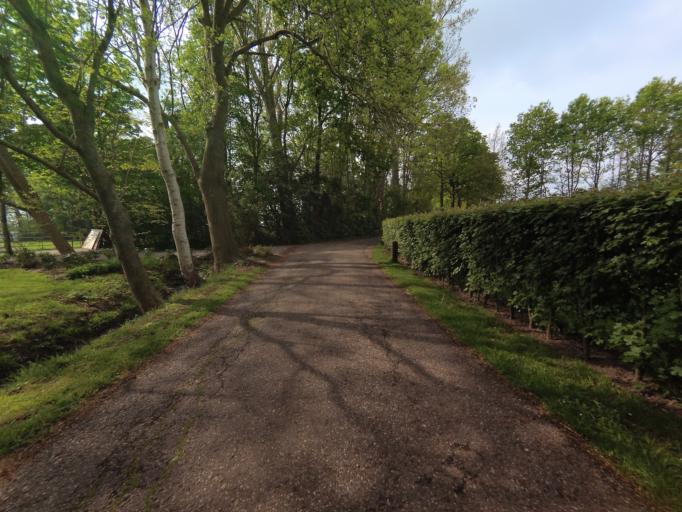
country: NL
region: Gelderland
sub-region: Gemeente Barneveld
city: Terschuur
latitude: 52.1364
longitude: 5.5206
